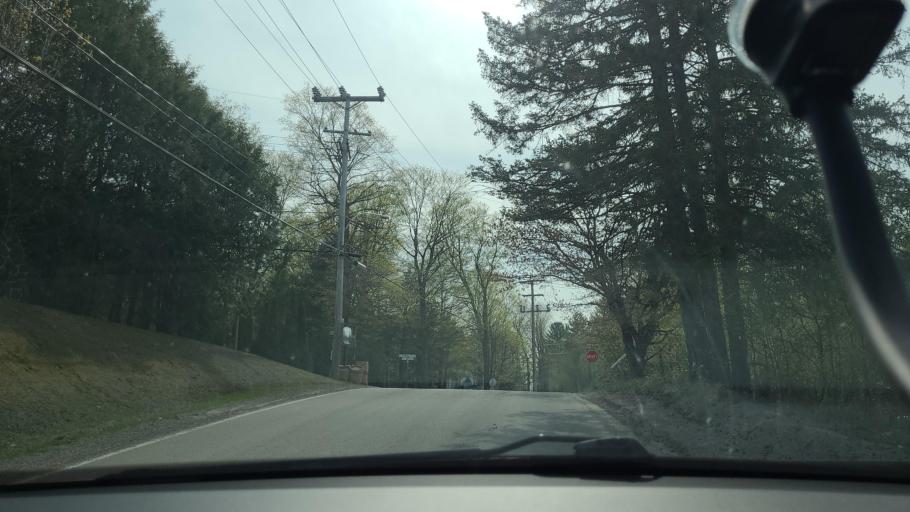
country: CA
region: Quebec
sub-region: Laurentides
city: Prevost
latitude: 45.8926
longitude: -74.0426
